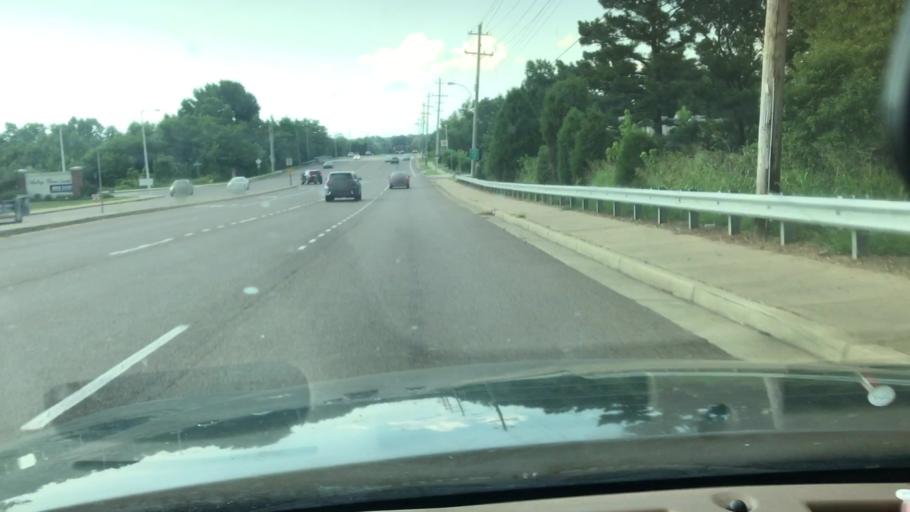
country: US
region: Tennessee
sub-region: Shelby County
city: Bartlett
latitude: 35.1878
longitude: -89.8137
